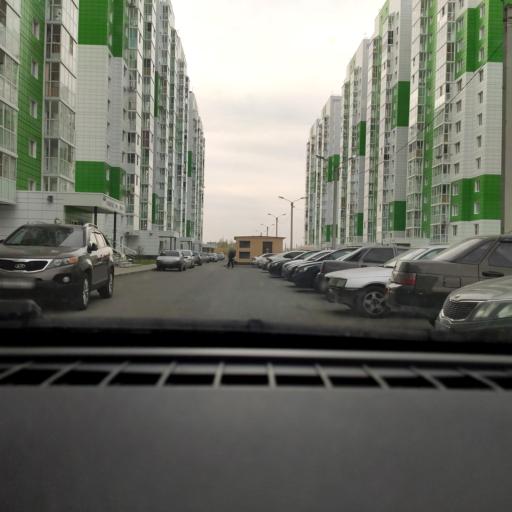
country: RU
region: Voronezj
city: Maslovka
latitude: 51.6358
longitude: 39.2963
